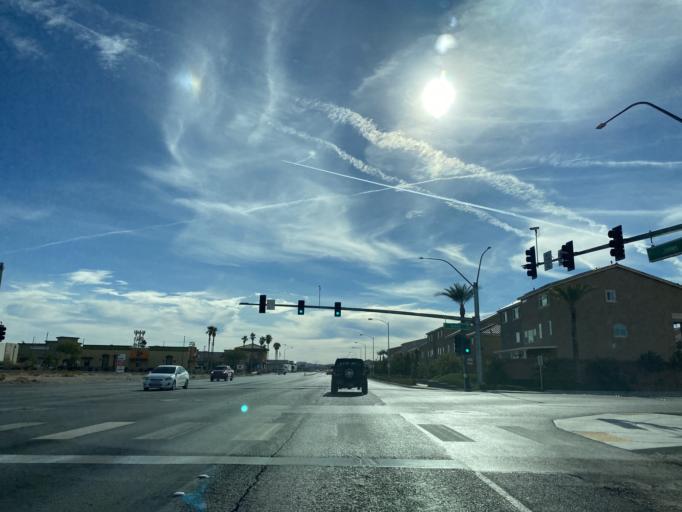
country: US
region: Nevada
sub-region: Clark County
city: Enterprise
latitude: 36.0623
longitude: -115.2247
